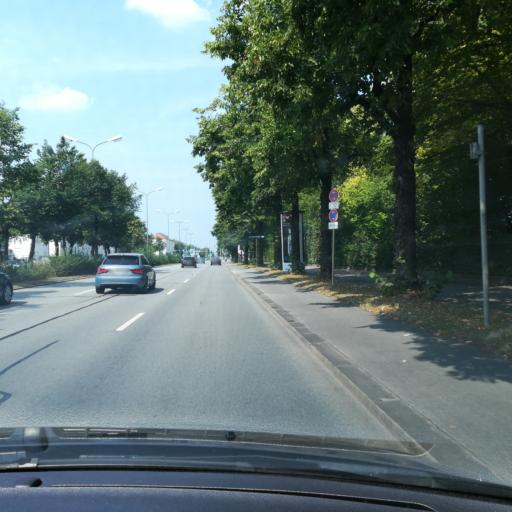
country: DE
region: Bavaria
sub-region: Upper Bavaria
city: Neuried
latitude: 48.1232
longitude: 11.5028
